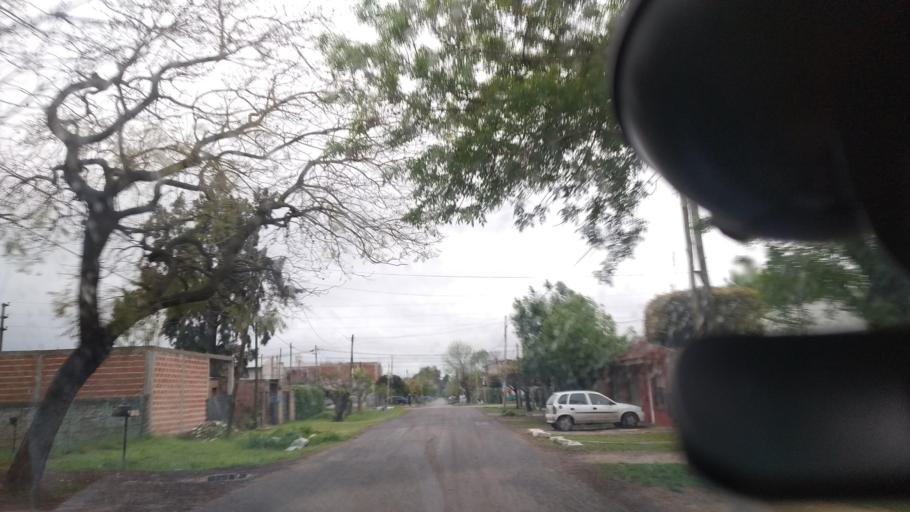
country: AR
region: Buenos Aires
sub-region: Partido de La Plata
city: La Plata
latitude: -34.9536
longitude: -57.9960
